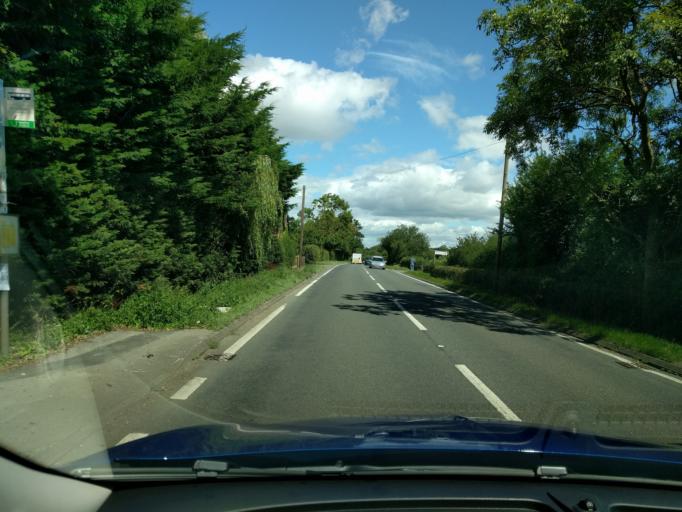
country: GB
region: England
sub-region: Warwickshire
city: Stratford-upon-Avon
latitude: 52.1453
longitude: -1.7383
